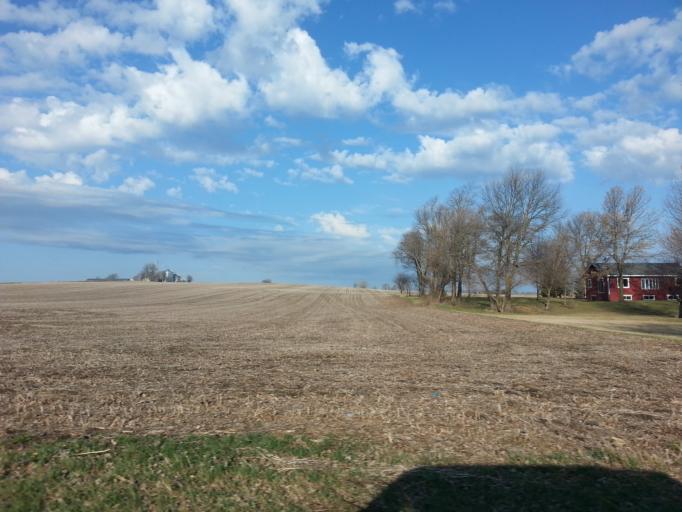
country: US
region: Minnesota
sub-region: Washington County
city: Afton
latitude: 44.8526
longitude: -92.8422
